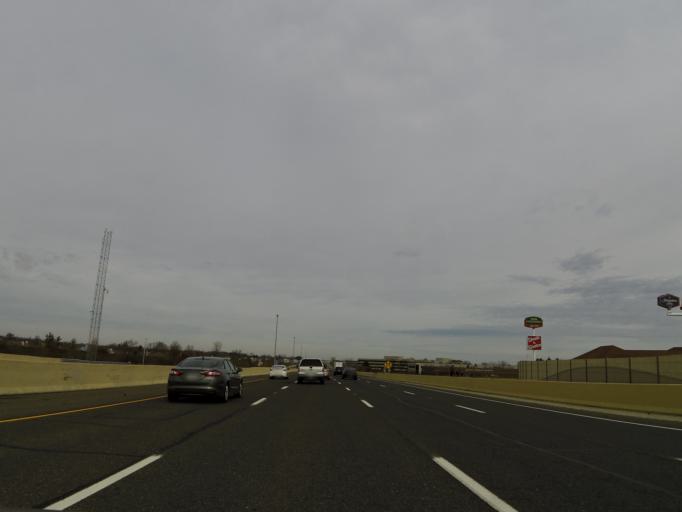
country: US
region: Indiana
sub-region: Boone County
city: Zionsville
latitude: 39.8826
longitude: -86.2690
